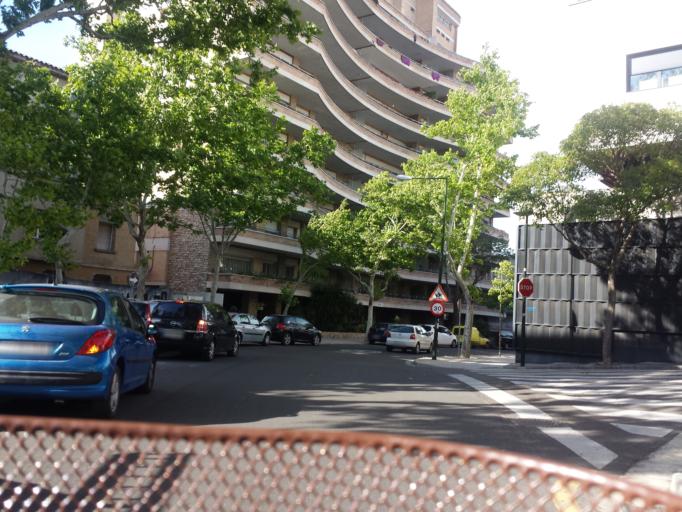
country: ES
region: Aragon
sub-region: Provincia de Zaragoza
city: Zaragoza
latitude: 41.6370
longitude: -0.8887
